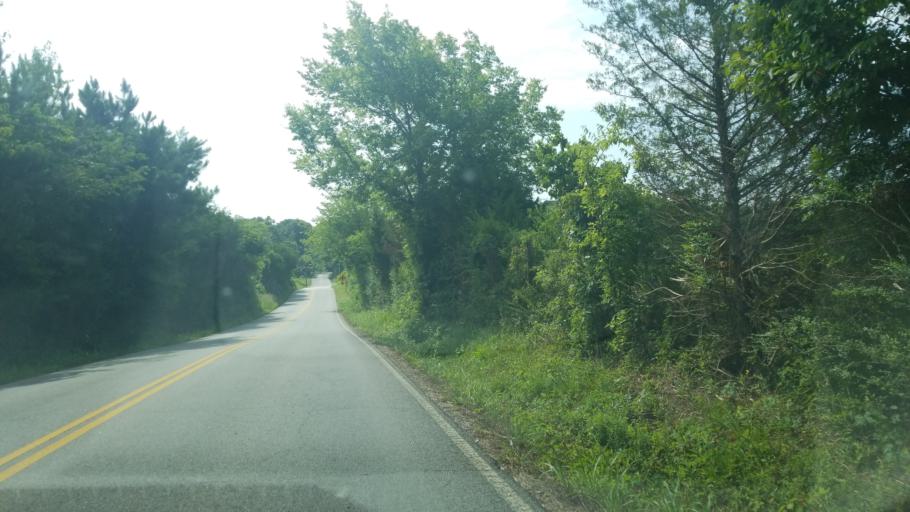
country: US
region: Tennessee
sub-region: Hamilton County
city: Apison
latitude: 35.0137
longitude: -85.0044
